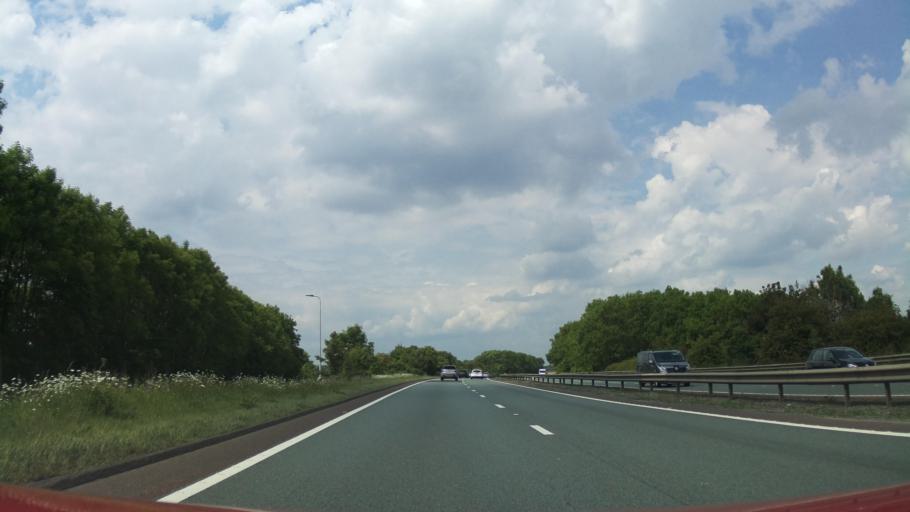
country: GB
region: England
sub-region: North Yorkshire
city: Thirsk
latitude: 54.2520
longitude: -1.3445
